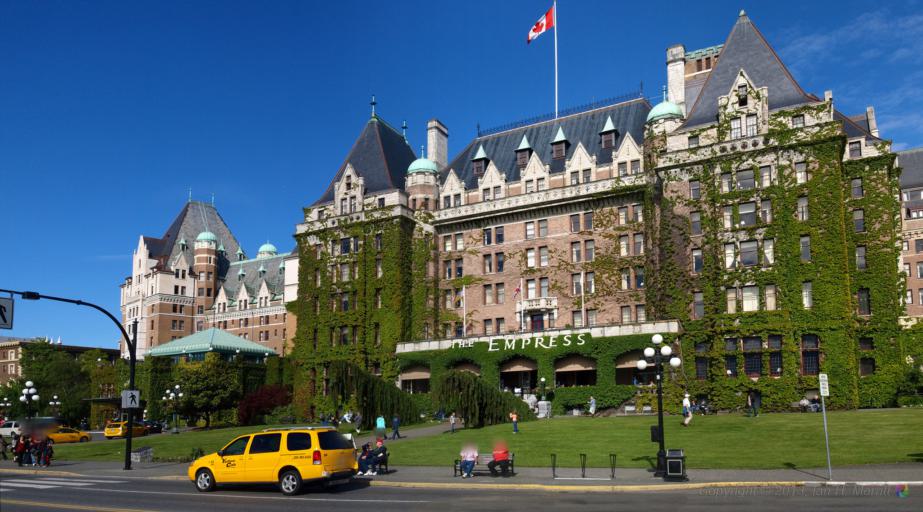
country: CA
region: British Columbia
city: Victoria
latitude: 48.4216
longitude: -123.3688
